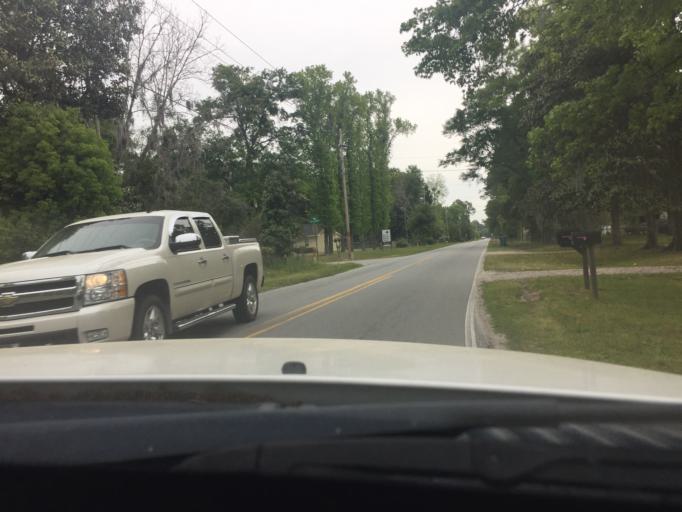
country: US
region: Georgia
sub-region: Chatham County
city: Georgetown
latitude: 31.9824
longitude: -81.2575
